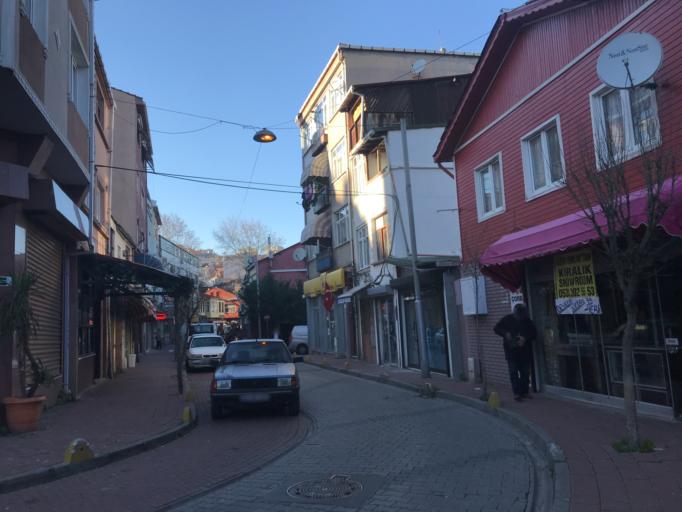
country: TR
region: Istanbul
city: Istanbul
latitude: 41.0257
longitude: 28.9571
